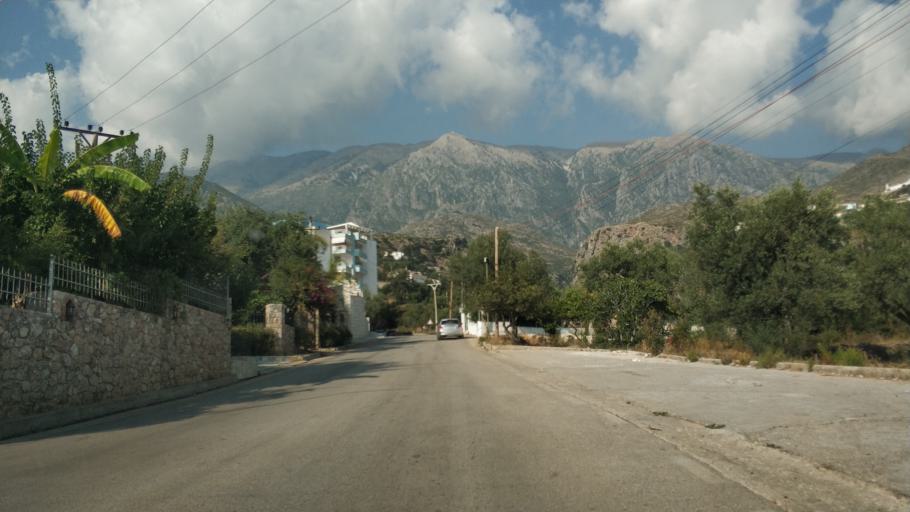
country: AL
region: Vlore
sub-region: Rrethi i Vlores
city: Vranisht
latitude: 40.1489
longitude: 19.6339
